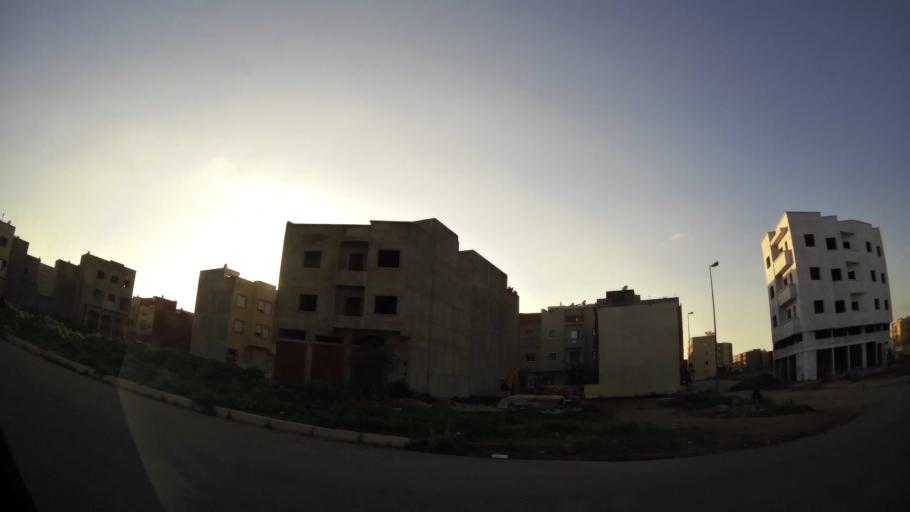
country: MA
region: Chaouia-Ouardigha
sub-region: Settat Province
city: Settat
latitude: 32.9853
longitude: -7.5966
